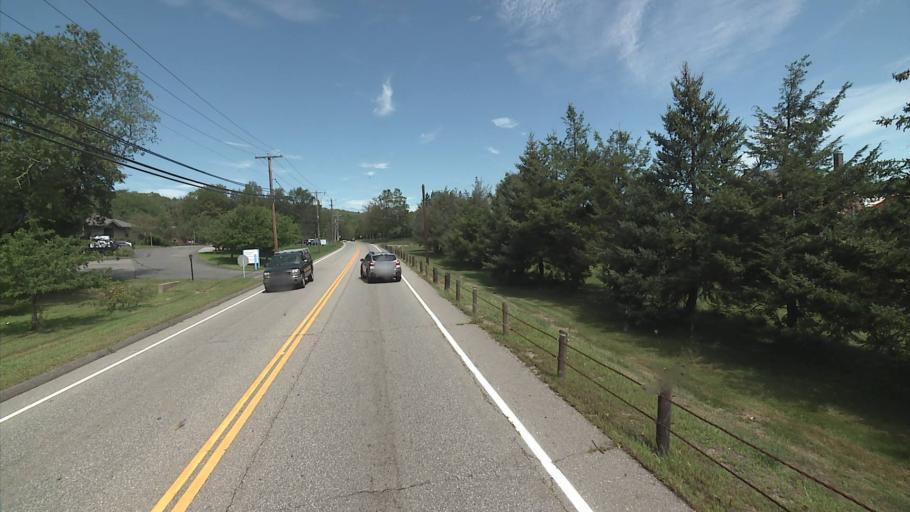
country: US
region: Connecticut
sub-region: Windham County
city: Willimantic
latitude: 41.7404
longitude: -72.1974
